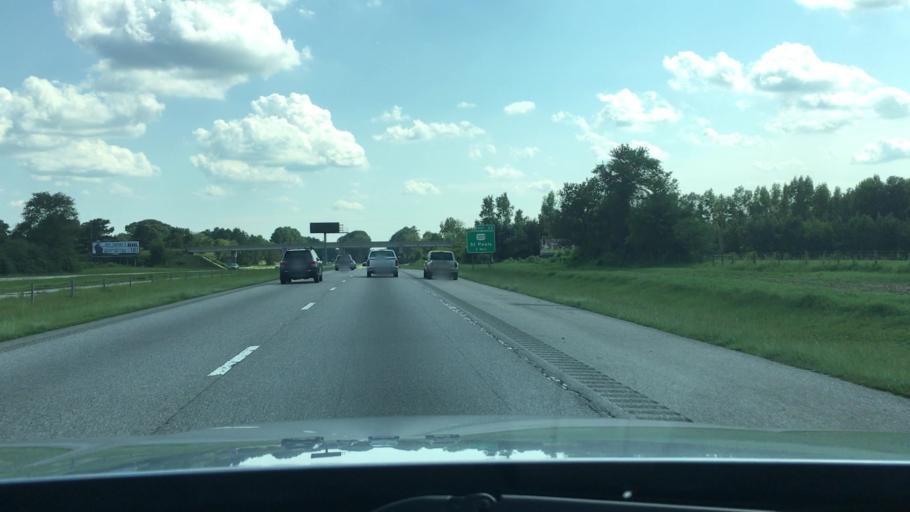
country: US
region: North Carolina
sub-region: Robeson County
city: Saint Pauls
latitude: 34.8496
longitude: -78.9692
